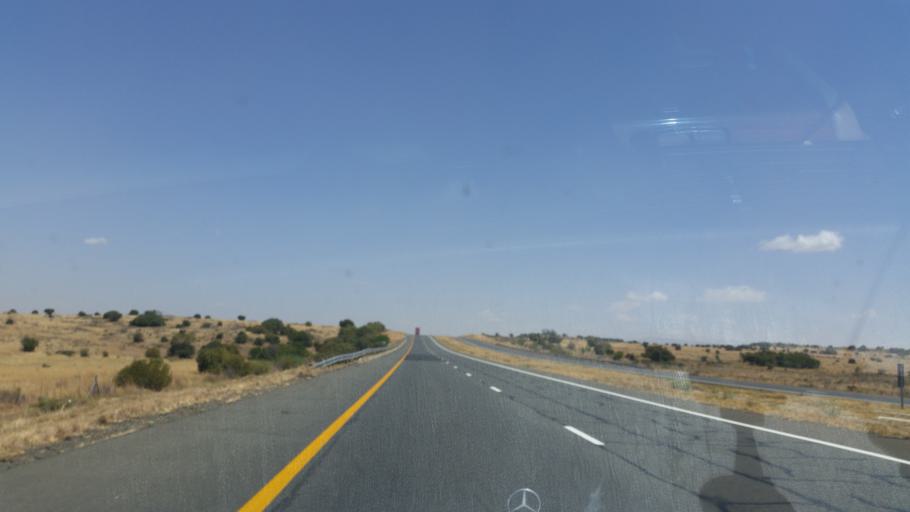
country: ZA
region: Orange Free State
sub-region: Lejweleputswa District Municipality
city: Brandfort
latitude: -28.9135
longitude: 26.4521
